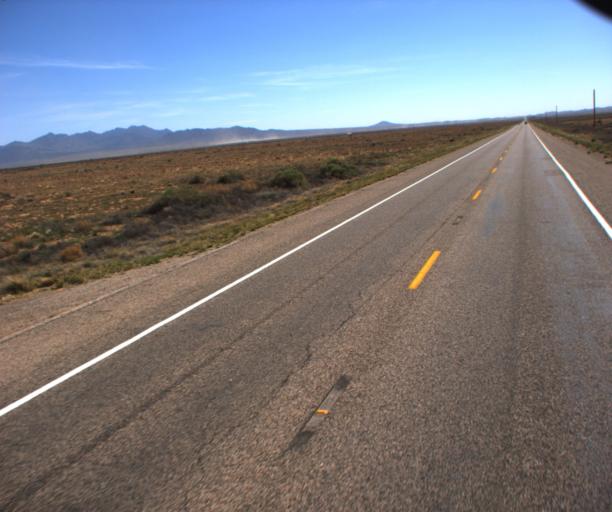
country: US
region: Arizona
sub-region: Mohave County
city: New Kingman-Butler
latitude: 35.3444
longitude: -113.8890
